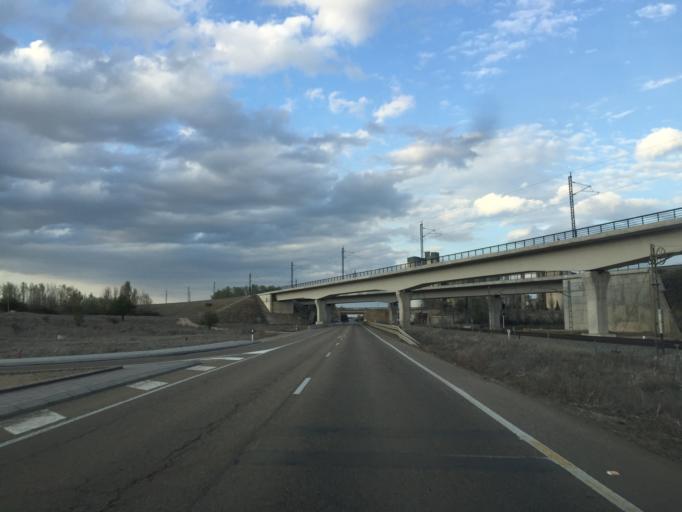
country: ES
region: Castille and Leon
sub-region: Provincia de Palencia
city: Venta de Banos
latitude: 41.9389
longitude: -4.4720
